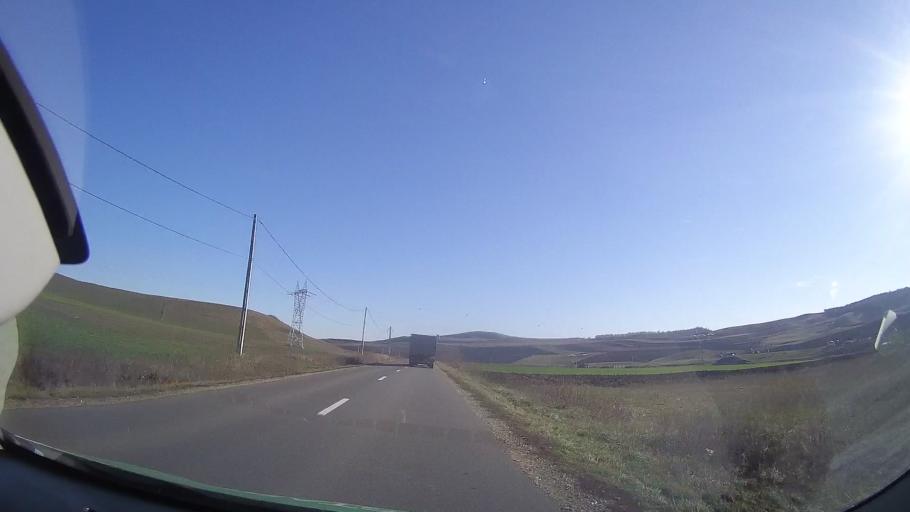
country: RO
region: Mures
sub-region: Comuna Mihesu de Campie
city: Mihesu de Campie
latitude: 46.6503
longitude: 24.1611
